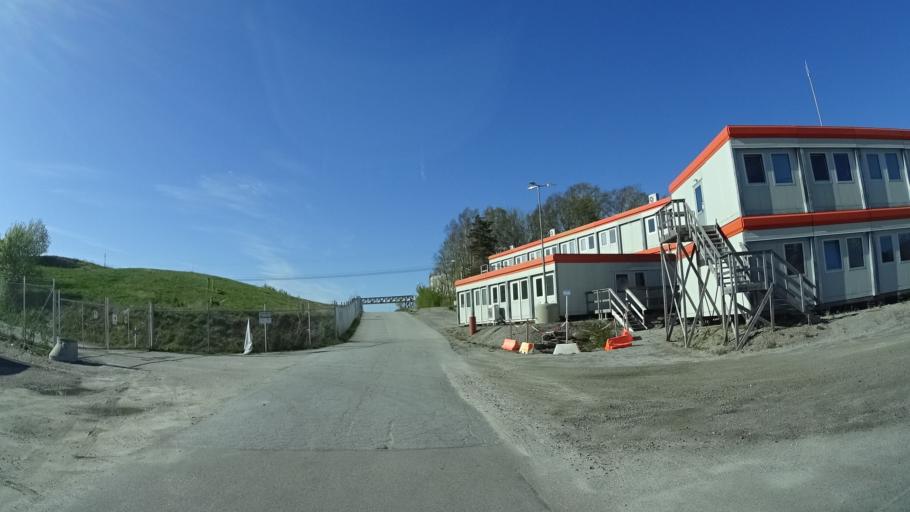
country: SE
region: Vaestra Goetaland
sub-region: Stenungsunds Kommun
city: Stenungsund
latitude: 58.0833
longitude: 11.8159
